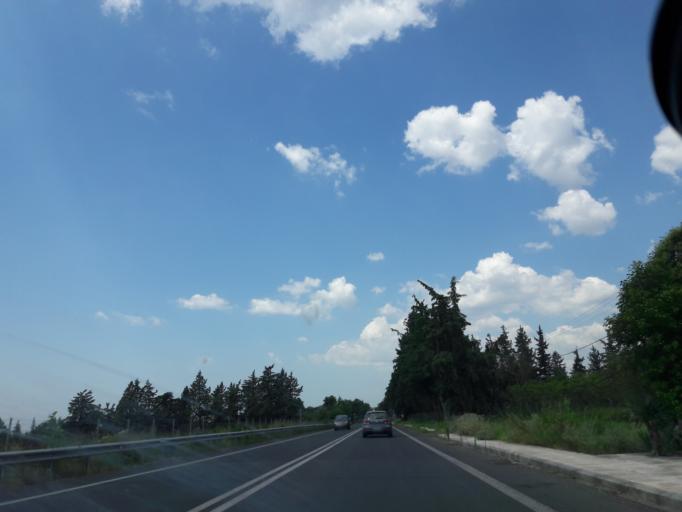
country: GR
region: Central Macedonia
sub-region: Nomos Thessalonikis
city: Souroti
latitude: 40.5098
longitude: 23.0828
